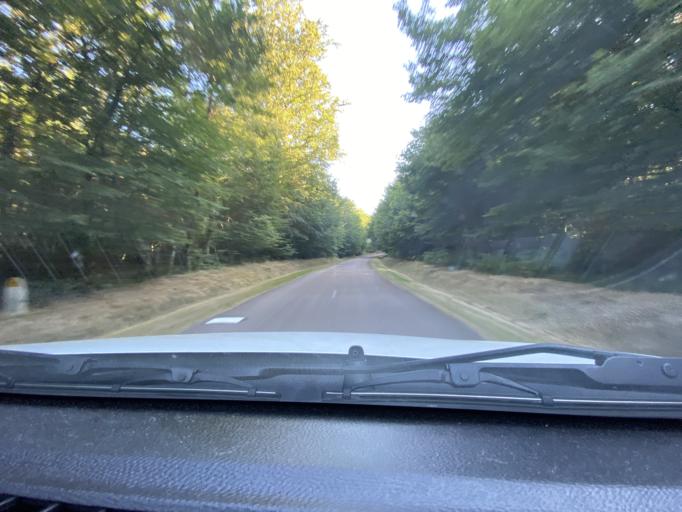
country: FR
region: Bourgogne
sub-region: Departement de la Cote-d'Or
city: Saulieu
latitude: 47.3014
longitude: 4.1772
